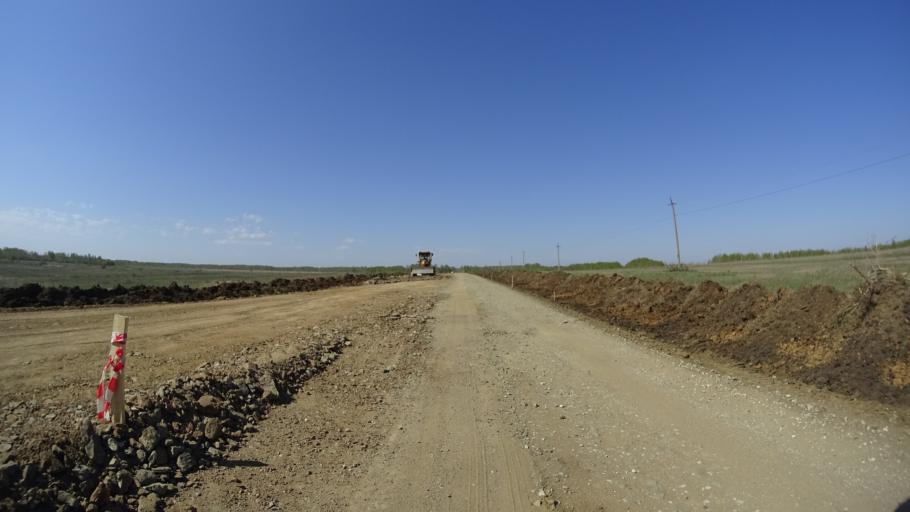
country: RU
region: Chelyabinsk
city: Troitsk
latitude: 54.1818
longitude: 61.4816
